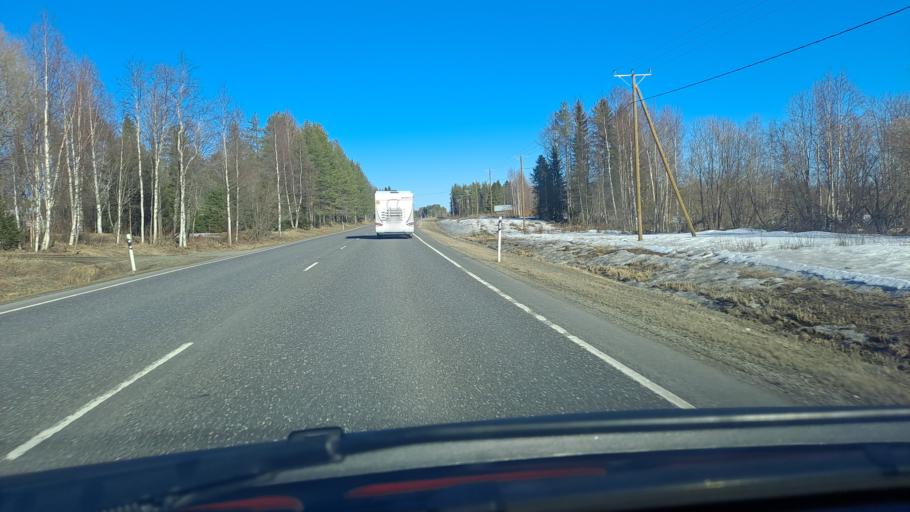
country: FI
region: Lapland
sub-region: Kemi-Tornio
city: Tervola
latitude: 66.1652
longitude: 25.1286
